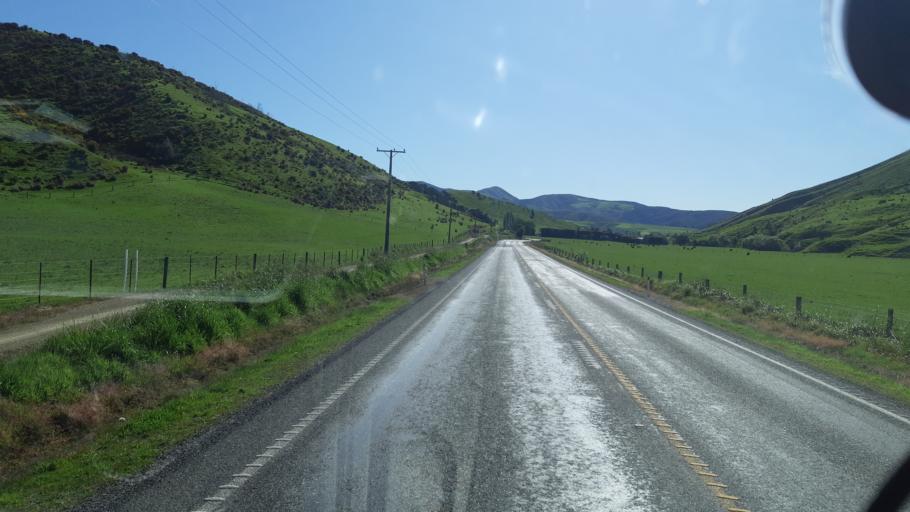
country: NZ
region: Otago
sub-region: Clutha District
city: Balclutha
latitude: -45.8293
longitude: 169.5548
